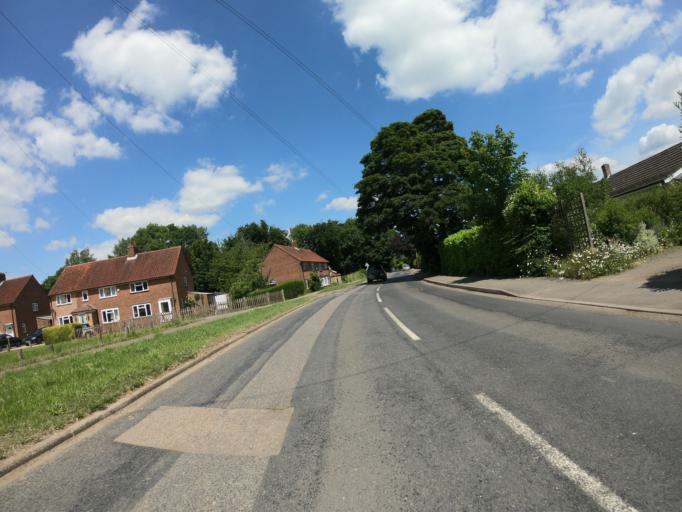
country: GB
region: England
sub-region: Kent
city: Halstead
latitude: 51.3278
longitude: 0.1324
